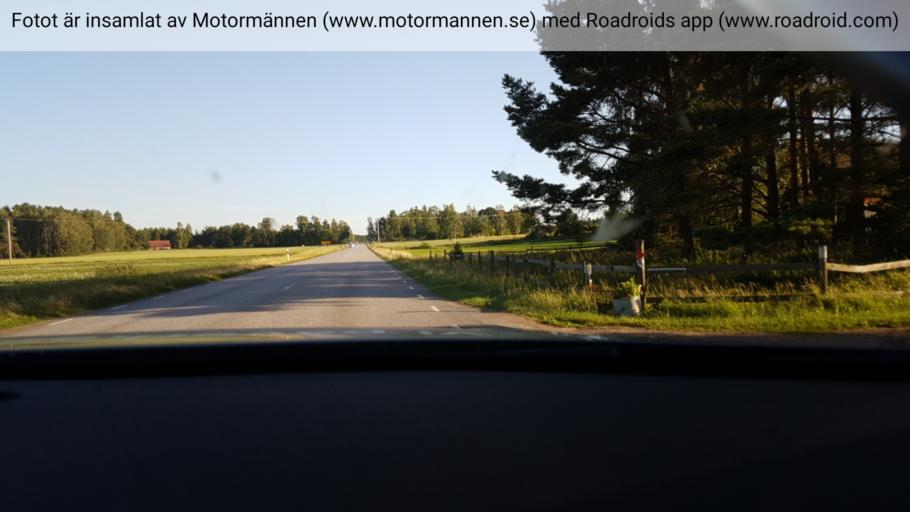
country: SE
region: Vaestra Goetaland
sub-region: Skovde Kommun
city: Stopen
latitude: 58.4850
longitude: 13.9589
